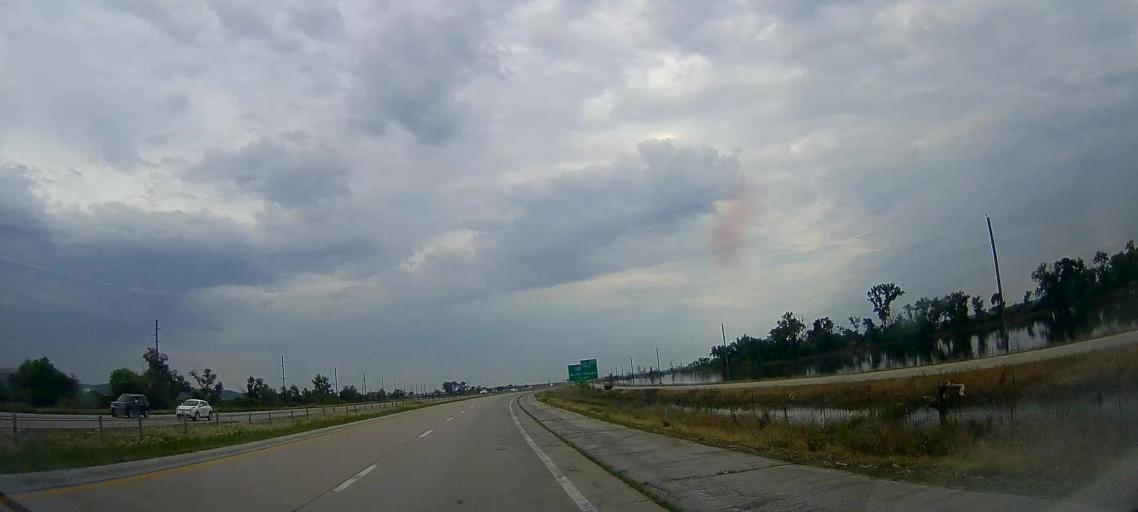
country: US
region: Iowa
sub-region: Pottawattamie County
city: Carter Lake
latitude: 41.3672
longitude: -95.8997
